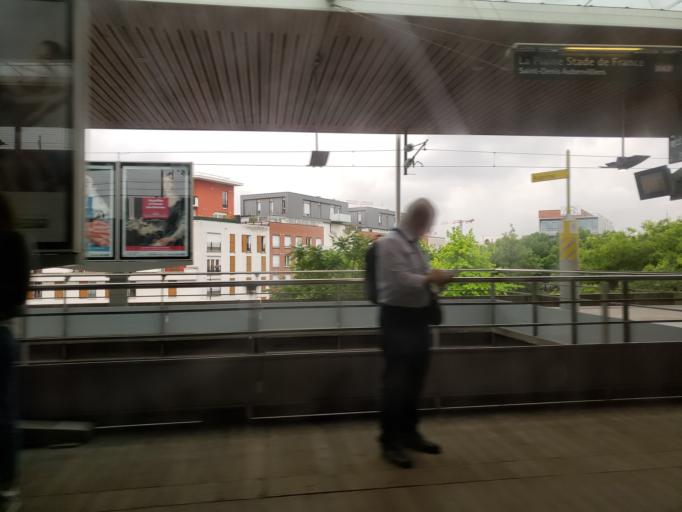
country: FR
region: Ile-de-France
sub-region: Departement de Seine-Saint-Denis
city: Saint-Denis
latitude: 48.9178
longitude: 2.3625
